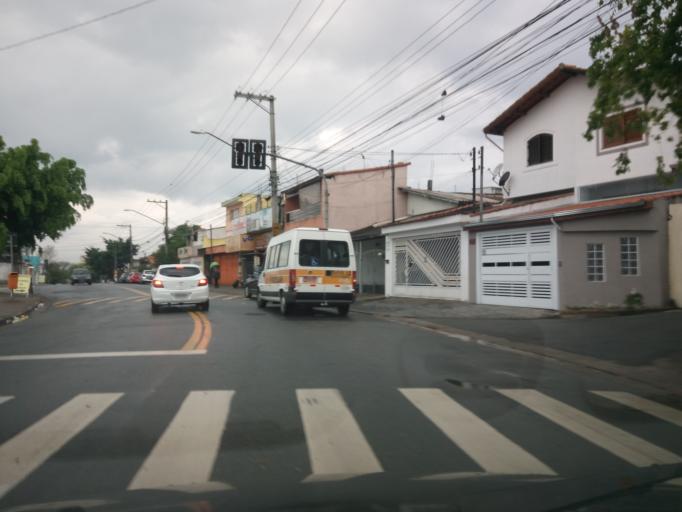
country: BR
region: Sao Paulo
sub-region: Sao Bernardo Do Campo
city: Sao Bernardo do Campo
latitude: -23.7225
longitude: -46.5854
